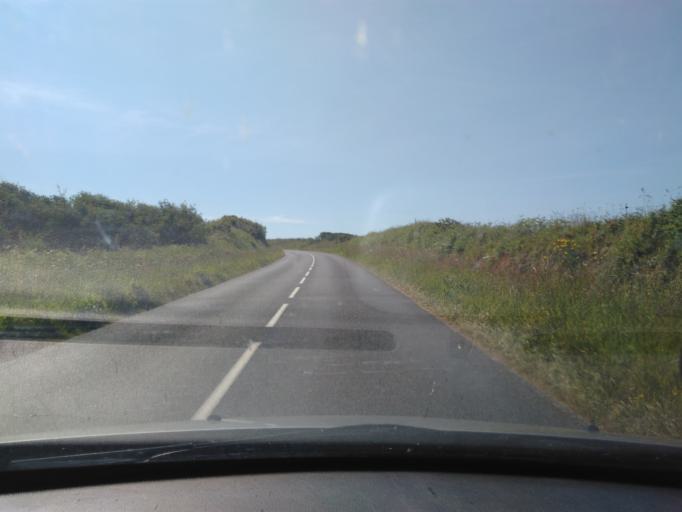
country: FR
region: Lower Normandy
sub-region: Departement de la Manche
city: Beaumont-Hague
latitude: 49.6987
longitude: -1.9260
